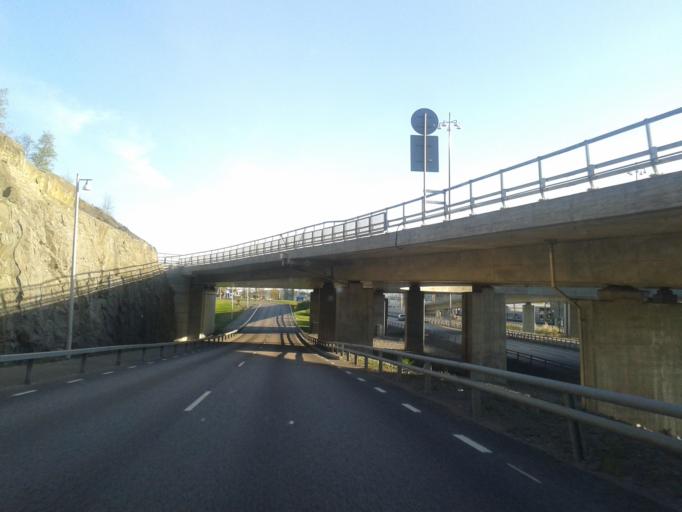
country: SE
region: Vaestra Goetaland
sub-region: Ale Kommun
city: Surte
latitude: 57.8547
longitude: 12.0157
